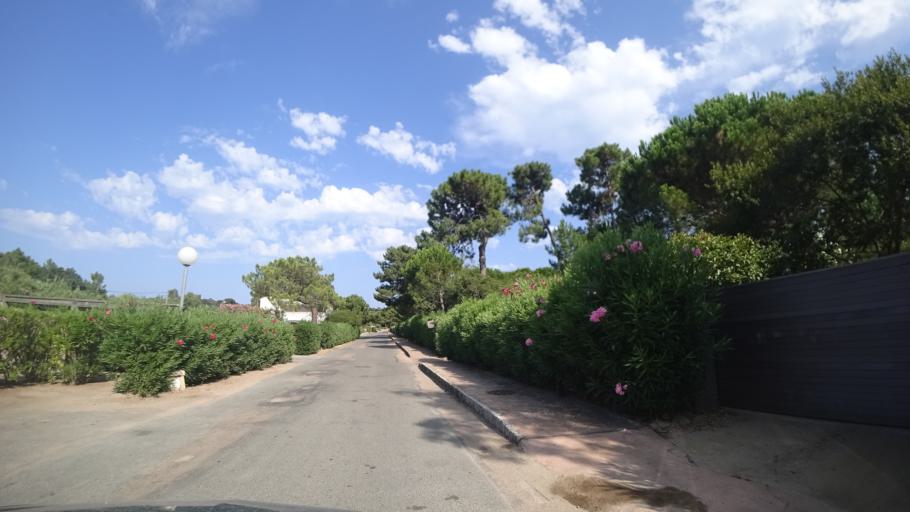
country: FR
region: Corsica
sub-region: Departement de la Corse-du-Sud
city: Porto-Vecchio
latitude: 41.6225
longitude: 9.3365
